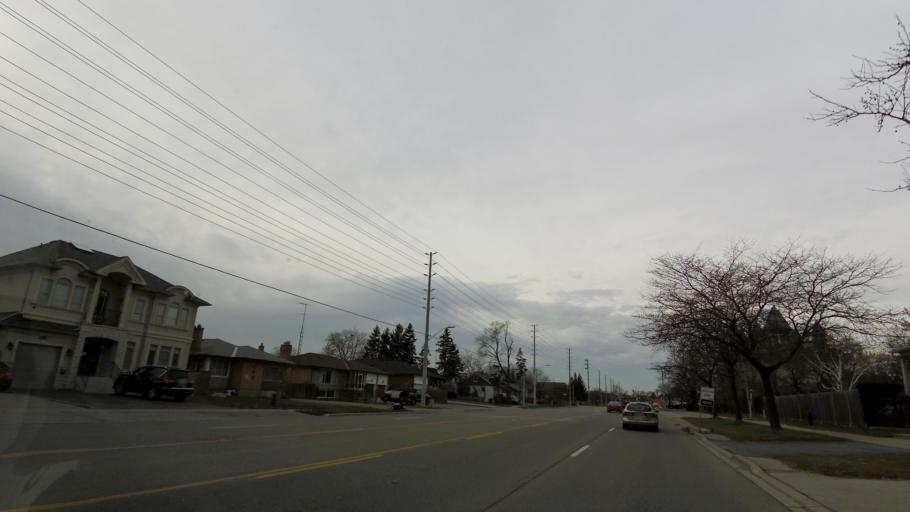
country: CA
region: Ontario
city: Mississauga
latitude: 43.6052
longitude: -79.6150
